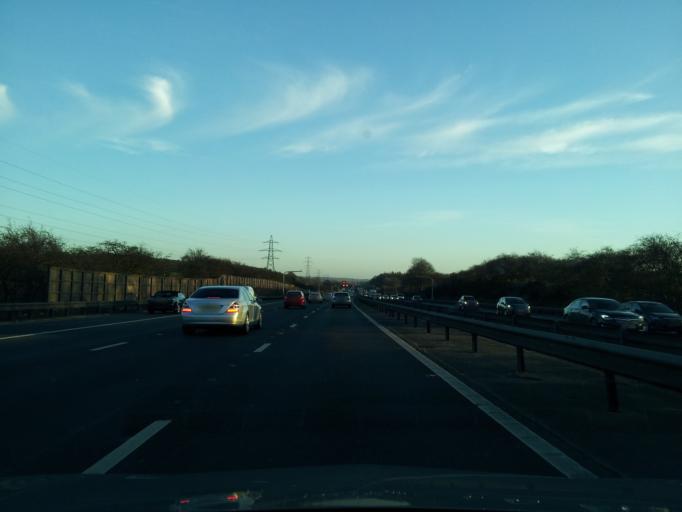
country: GB
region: England
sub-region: Central Bedfordshire
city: Steppingley
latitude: 52.0054
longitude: -0.5471
